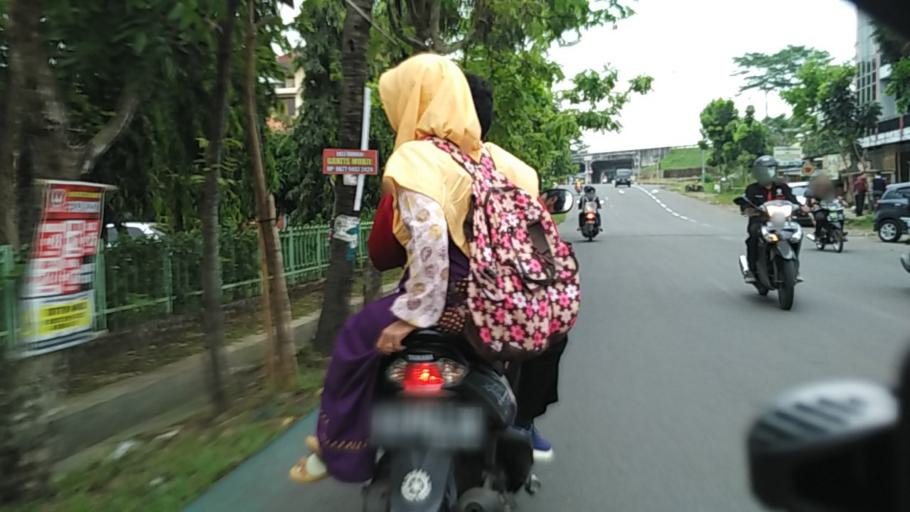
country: ID
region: Central Java
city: Semarang
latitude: -7.0636
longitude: 110.4265
